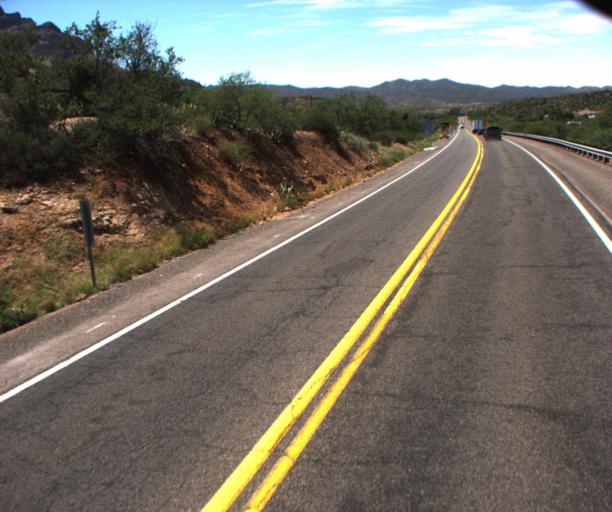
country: US
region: Arizona
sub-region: Pinal County
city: Superior
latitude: 33.2841
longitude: -111.1447
